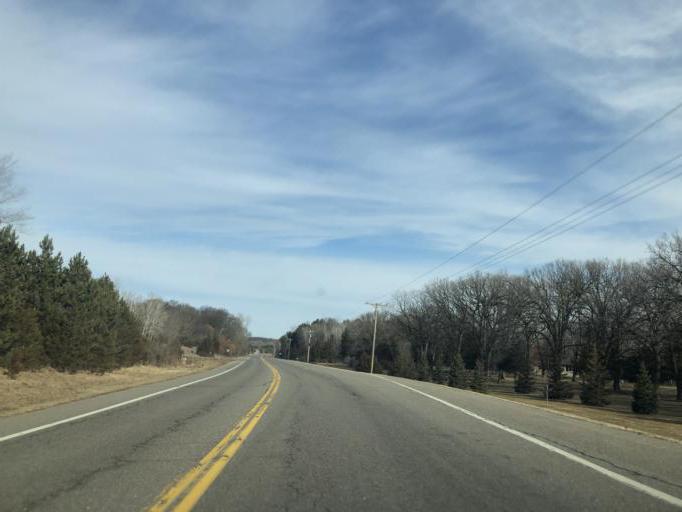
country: US
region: Minnesota
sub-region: Sherburne County
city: Becker
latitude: 45.4203
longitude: -93.8714
